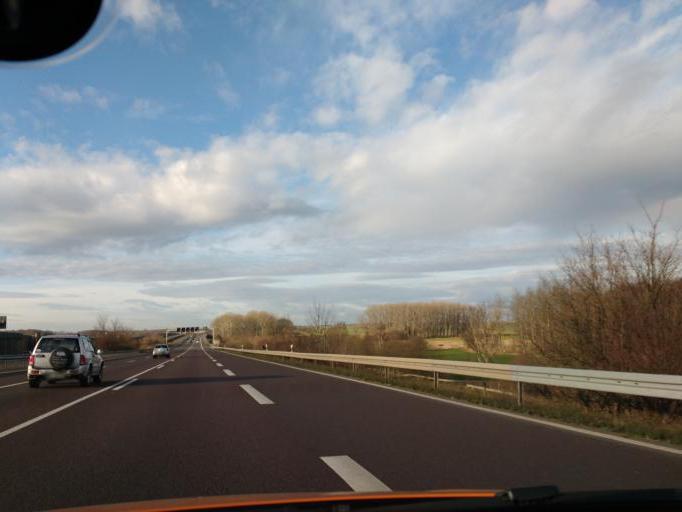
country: DE
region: Lower Saxony
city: Konigslutter am Elm
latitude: 52.3117
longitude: 10.8122
